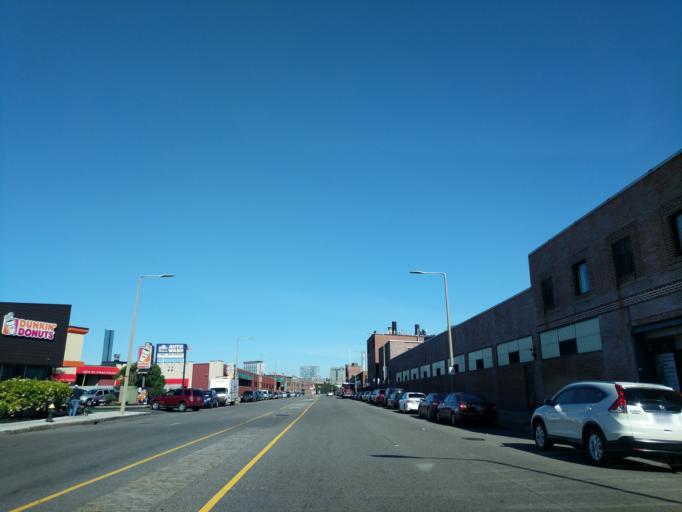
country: US
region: Massachusetts
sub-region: Suffolk County
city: South Boston
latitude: 42.3356
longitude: -71.0555
